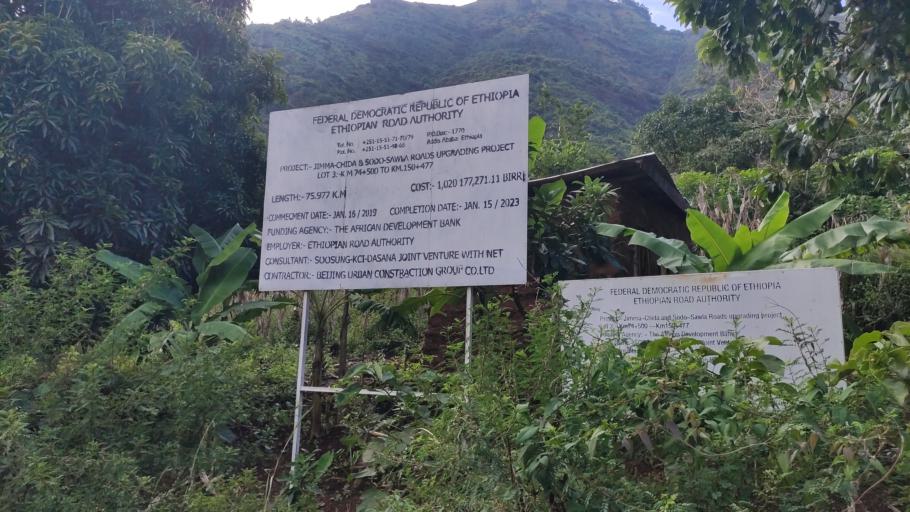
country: ET
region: Southern Nations, Nationalities, and People's Region
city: Arba Minch'
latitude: 6.4459
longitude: 37.3955
